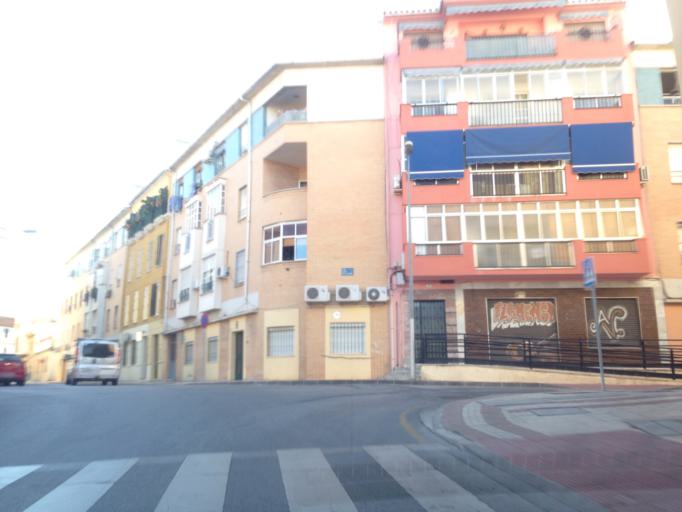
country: ES
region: Andalusia
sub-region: Provincia de Malaga
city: Malaga
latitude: 36.7297
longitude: -4.4234
